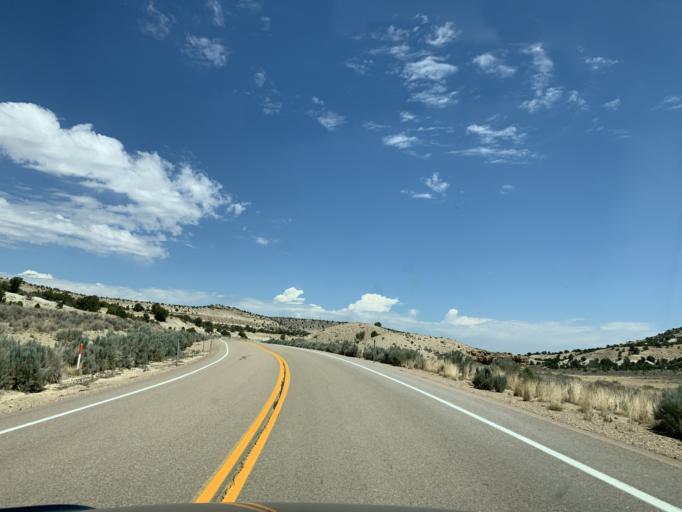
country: US
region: Utah
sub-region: Duchesne County
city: Duchesne
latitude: 39.9546
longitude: -110.1911
